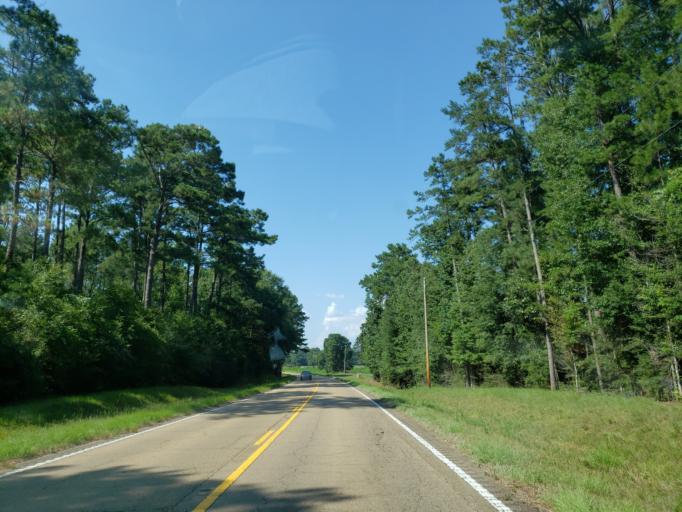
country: US
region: Mississippi
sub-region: Lamar County
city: Sumrall
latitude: 31.4468
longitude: -89.5286
